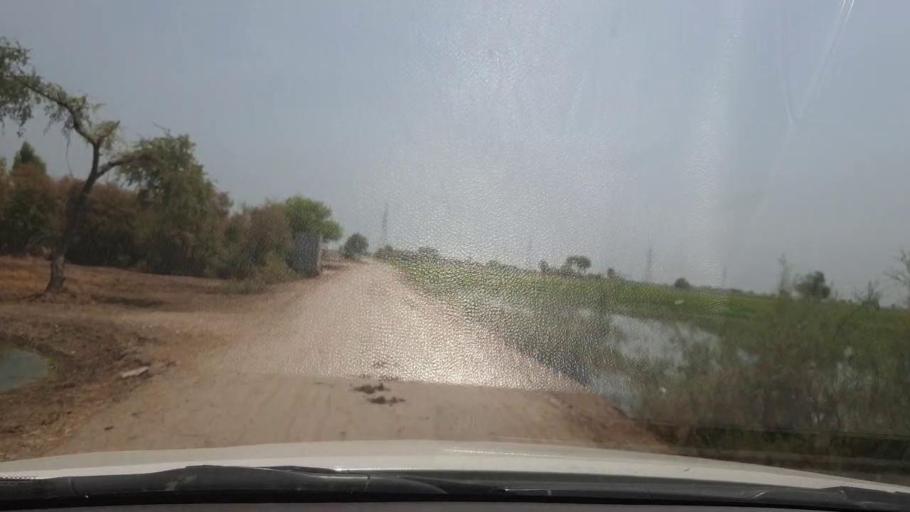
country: PK
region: Sindh
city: Shikarpur
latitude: 28.0955
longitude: 68.6117
